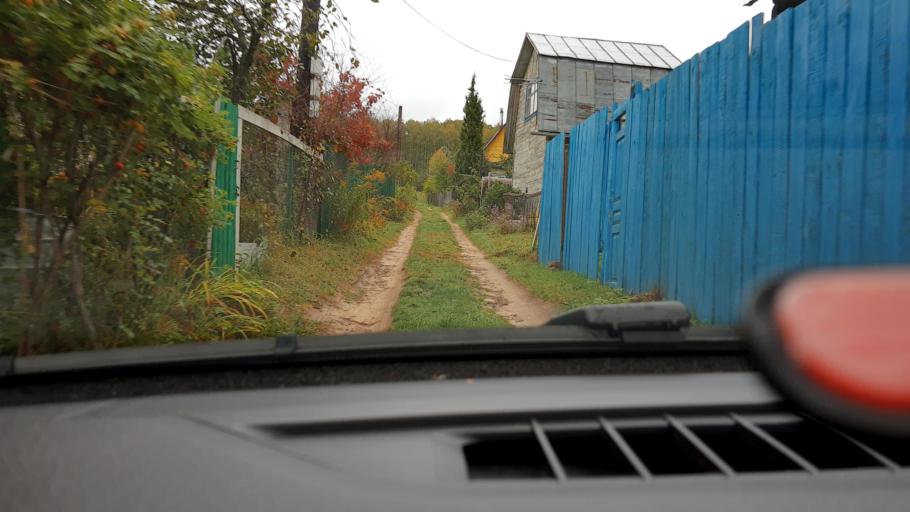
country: RU
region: Nizjnij Novgorod
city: Burevestnik
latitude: 56.1026
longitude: 43.9521
